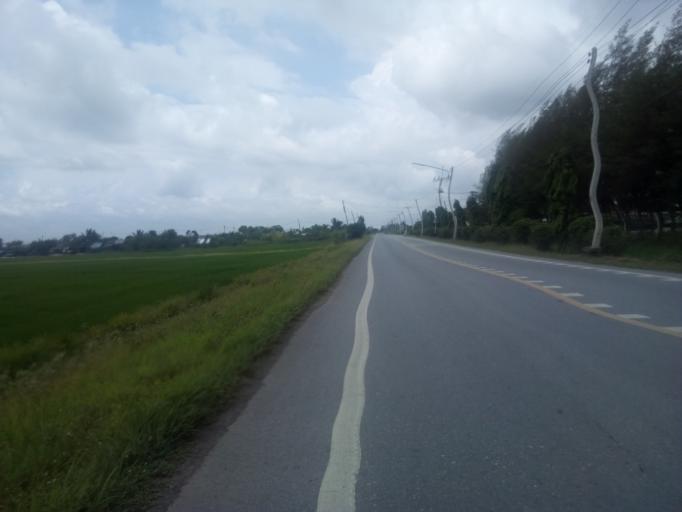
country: TH
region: Pathum Thani
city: Ban Lam Luk Ka
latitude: 14.0093
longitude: 100.8227
